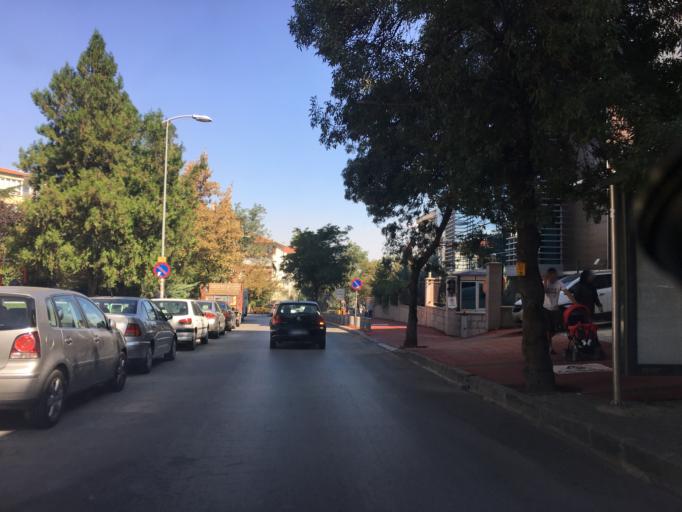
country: TR
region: Ankara
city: Ankara
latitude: 39.8990
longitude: 32.8506
